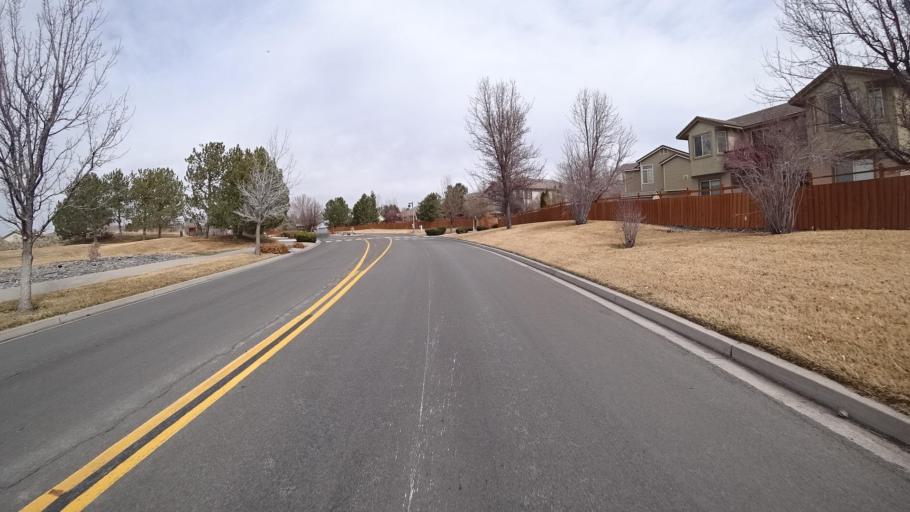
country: US
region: Nevada
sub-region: Washoe County
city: Spanish Springs
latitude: 39.6187
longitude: -119.6795
